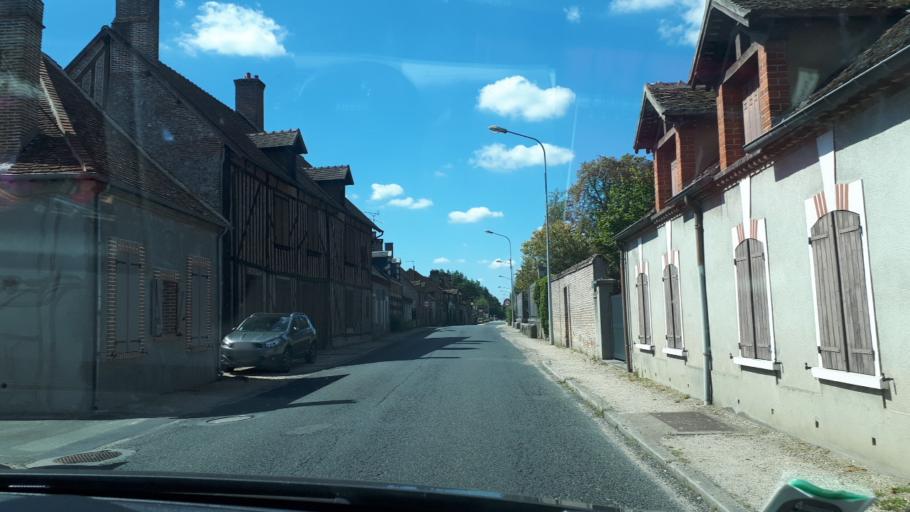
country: FR
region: Centre
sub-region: Departement du Loir-et-Cher
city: Neung-sur-Beuvron
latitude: 47.5421
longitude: 1.8486
